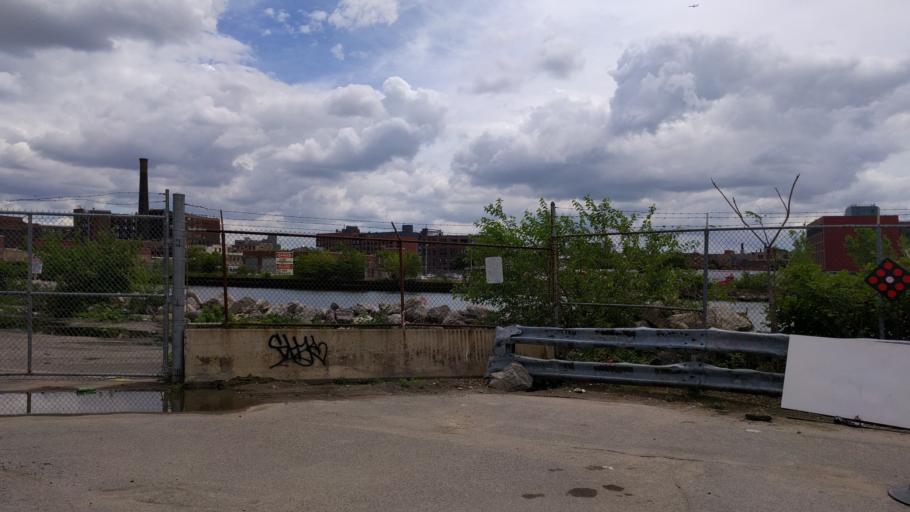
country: US
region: New York
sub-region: Queens County
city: Long Island City
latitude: 40.7387
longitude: -73.9600
